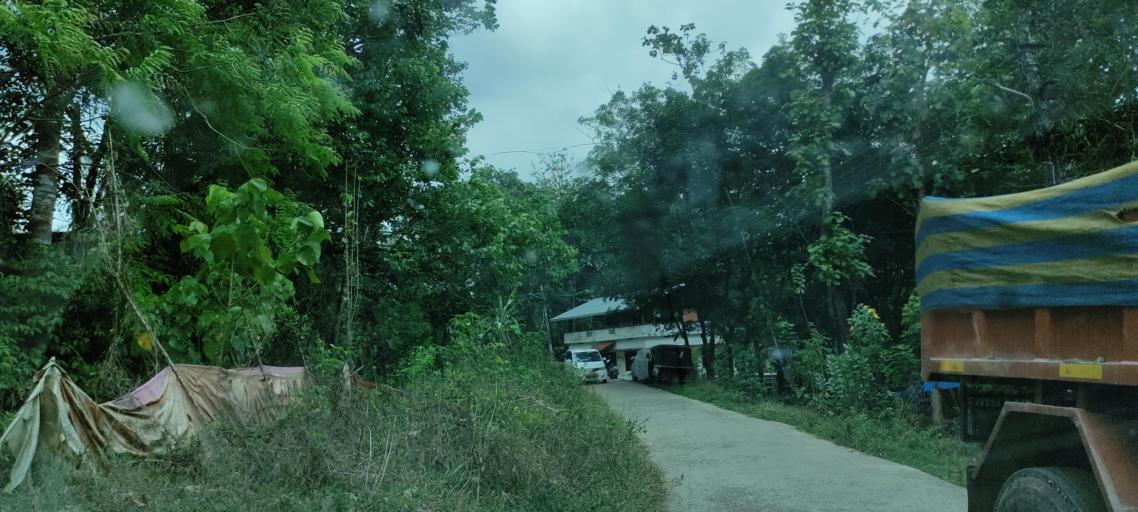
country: IN
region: Kerala
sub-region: Pattanamtitta
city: Adur
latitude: 9.1703
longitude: 76.7460
